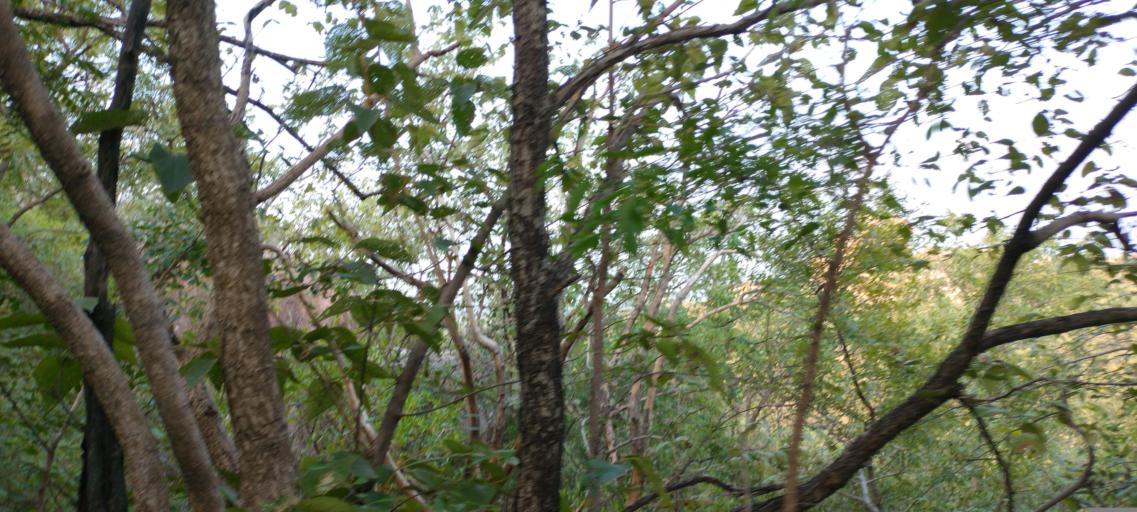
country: IN
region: Telangana
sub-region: Mahbubnagar
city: Farrukhnagar
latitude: 16.8947
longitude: 78.4954
